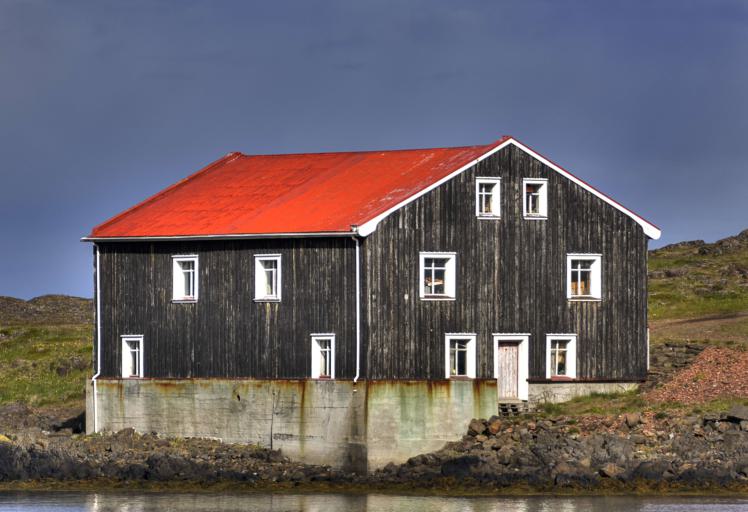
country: IS
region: East
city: Reydarfjoerdur
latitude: 64.6576
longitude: -14.2821
